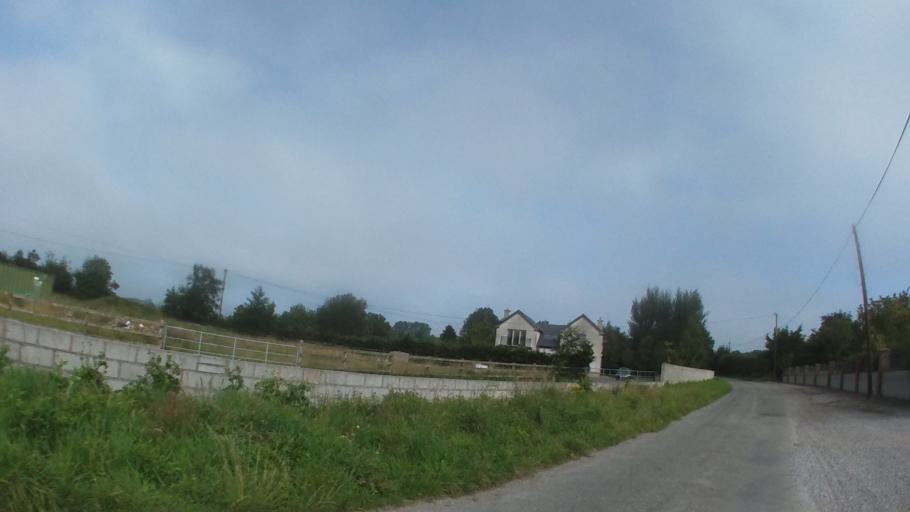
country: IE
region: Leinster
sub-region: Kilkenny
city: Kilkenny
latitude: 52.6882
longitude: -7.1875
